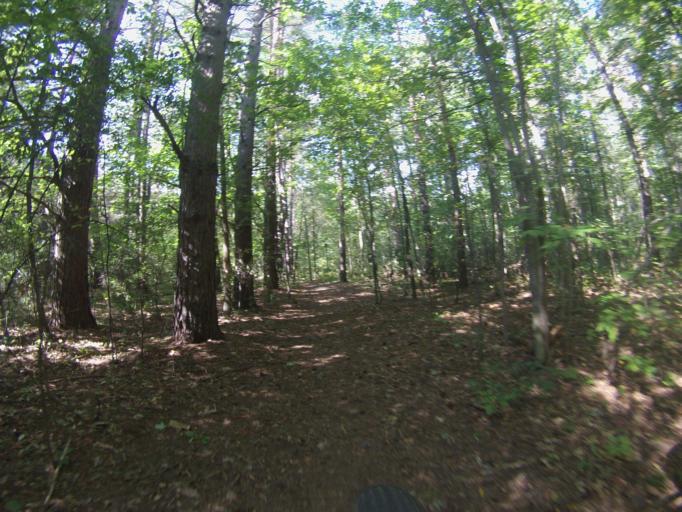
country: CA
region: Ontario
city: Ottawa
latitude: 45.3546
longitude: -75.6221
